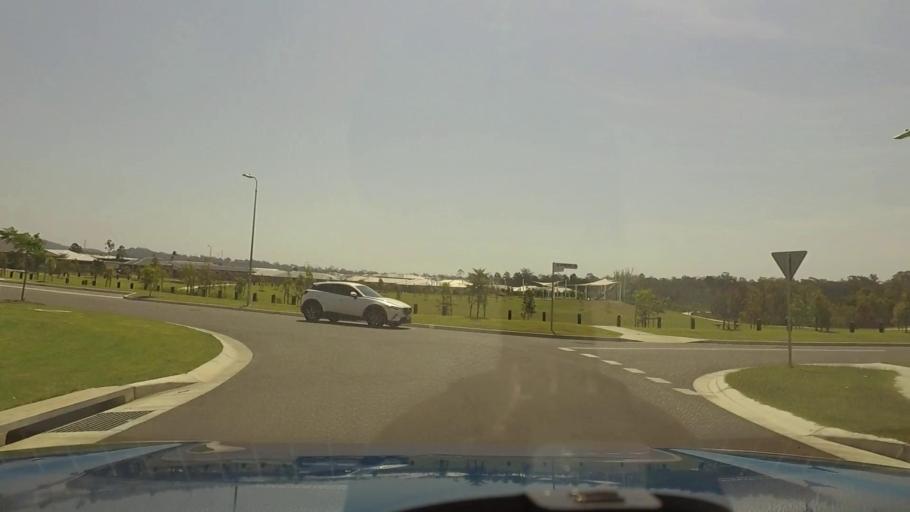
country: AU
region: Queensland
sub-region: Logan
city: Chambers Flat
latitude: -27.7996
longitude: 153.1193
